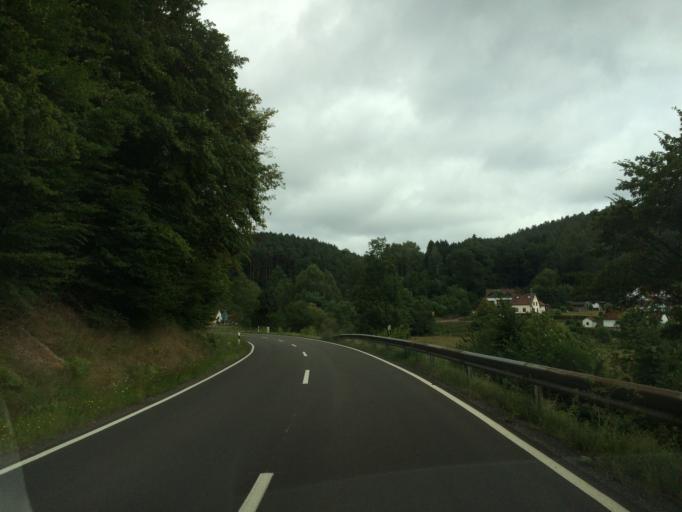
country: DE
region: Rheinland-Pfalz
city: Ruppertsweiler
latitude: 49.1666
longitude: 7.7172
